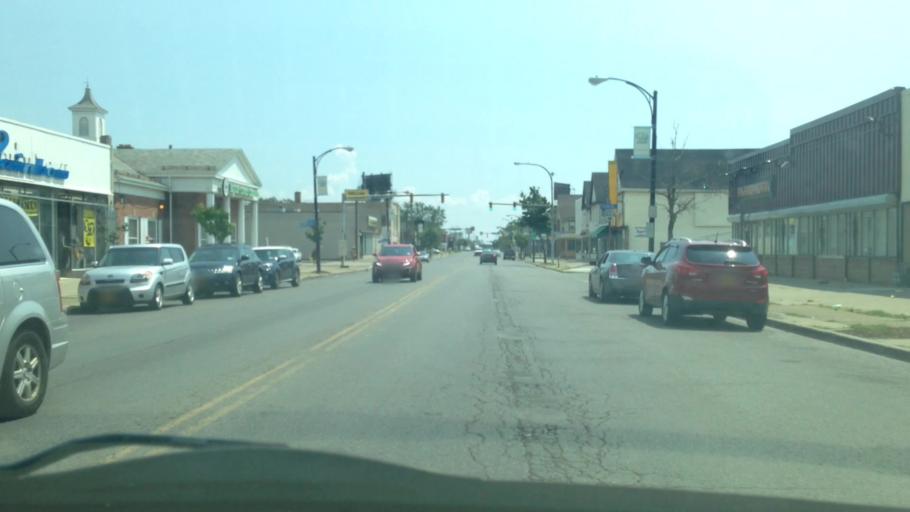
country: US
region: New York
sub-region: Erie County
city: Eggertsville
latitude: 42.9399
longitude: -78.8137
